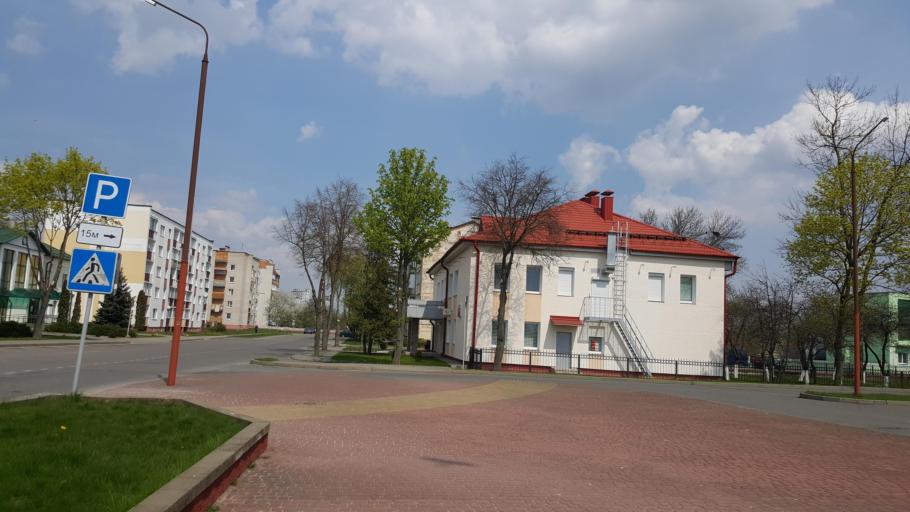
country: BY
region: Brest
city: Zhabinka
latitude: 52.1948
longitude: 24.0198
